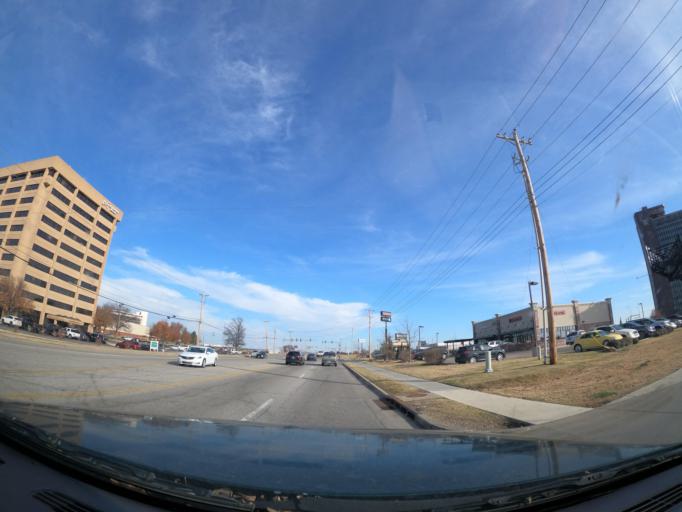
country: US
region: Oklahoma
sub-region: Tulsa County
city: Tulsa
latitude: 36.1043
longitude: -95.9119
